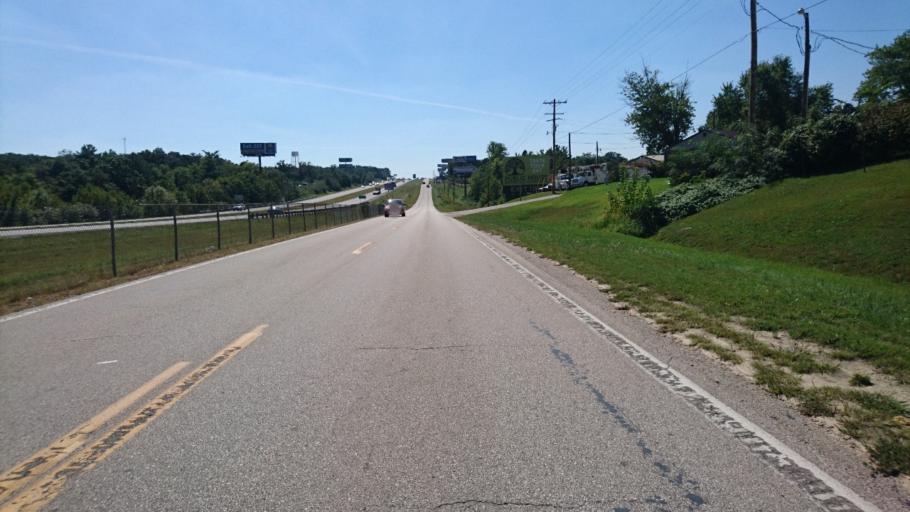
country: US
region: Missouri
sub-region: Franklin County
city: Sullivan
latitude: 38.2346
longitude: -91.1474
